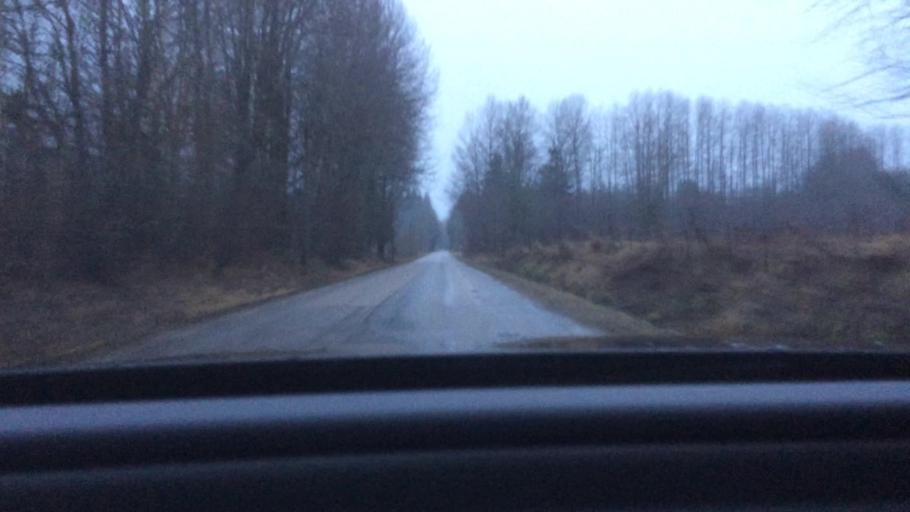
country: SE
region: Vaestra Goetaland
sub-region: Ulricehamns Kommun
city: Ulricehamn
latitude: 57.9606
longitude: 13.3964
